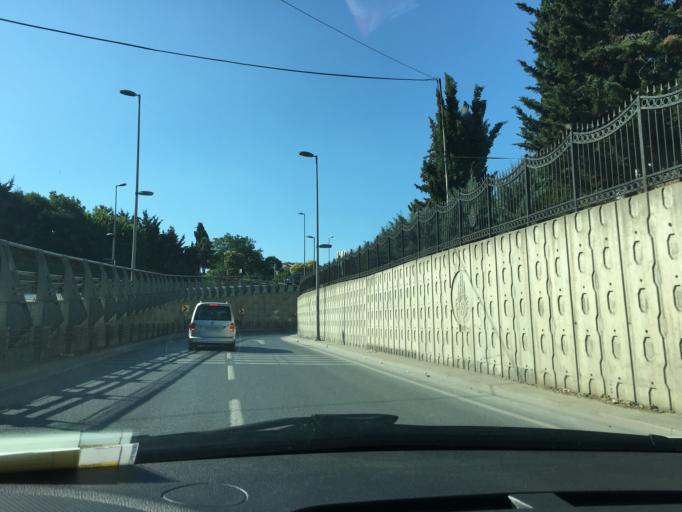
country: TR
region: Istanbul
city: Sisli
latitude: 41.0513
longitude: 28.9698
